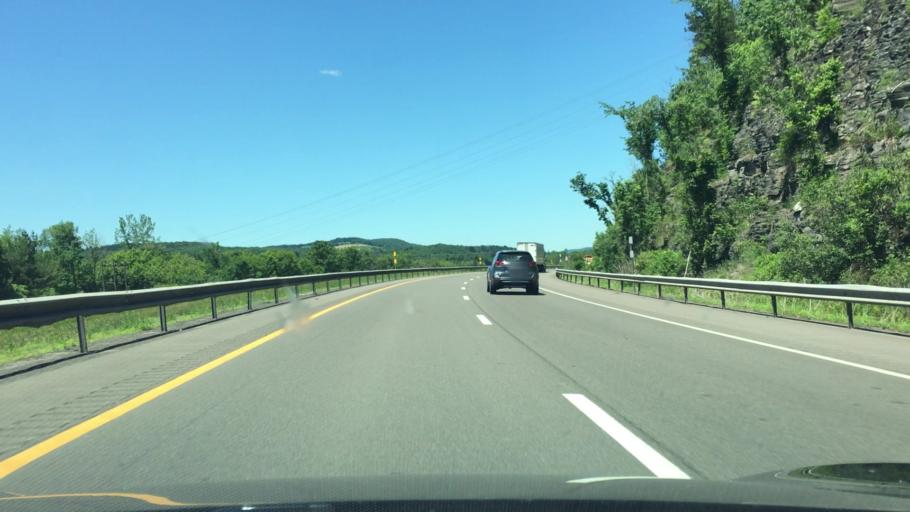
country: US
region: New York
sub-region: Cortland County
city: Cortland
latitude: 42.6116
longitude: -76.1800
